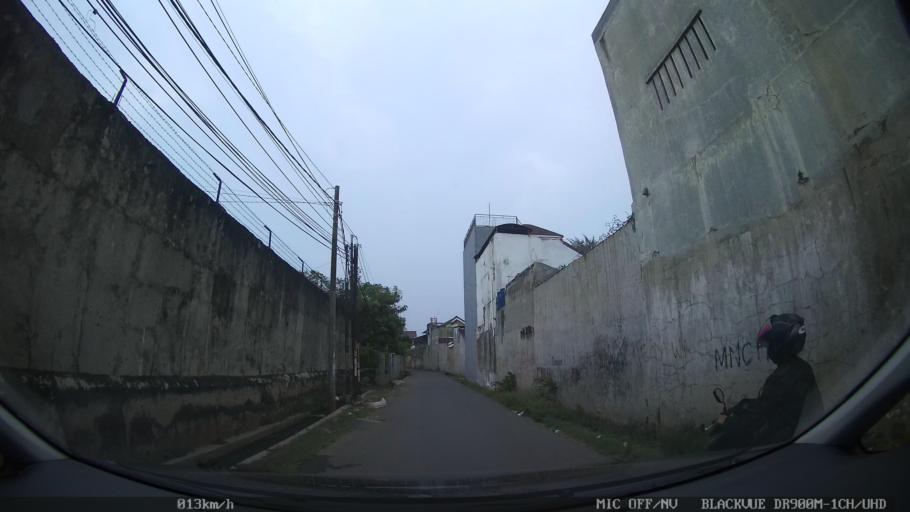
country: ID
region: Lampung
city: Kedaton
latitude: -5.4030
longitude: 105.2719
